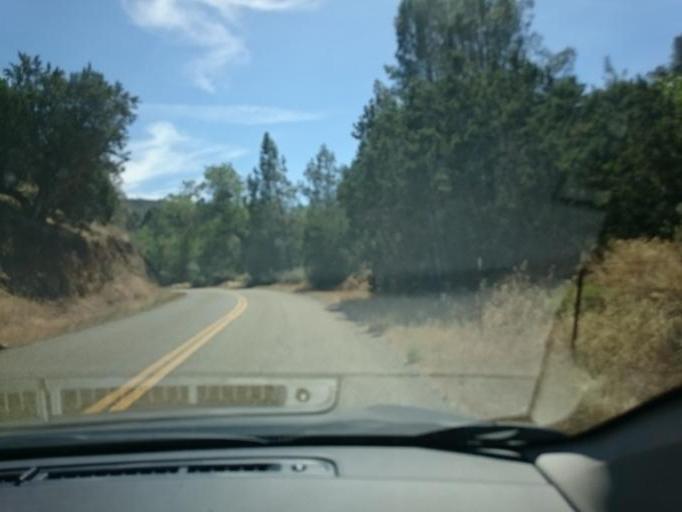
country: US
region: California
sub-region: Stanislaus County
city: Patterson
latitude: 37.4263
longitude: -121.3411
